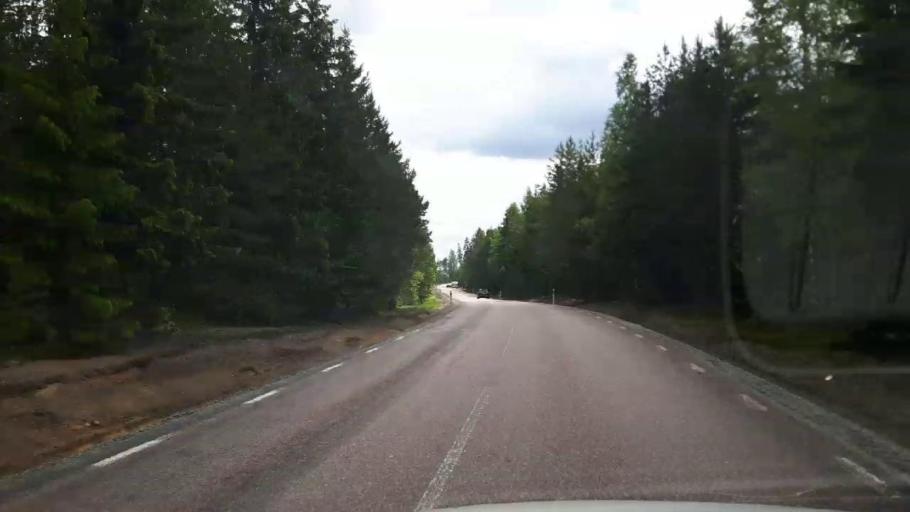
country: SE
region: Vaestmanland
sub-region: Skinnskattebergs Kommun
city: Skinnskatteberg
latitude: 59.8288
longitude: 15.8326
